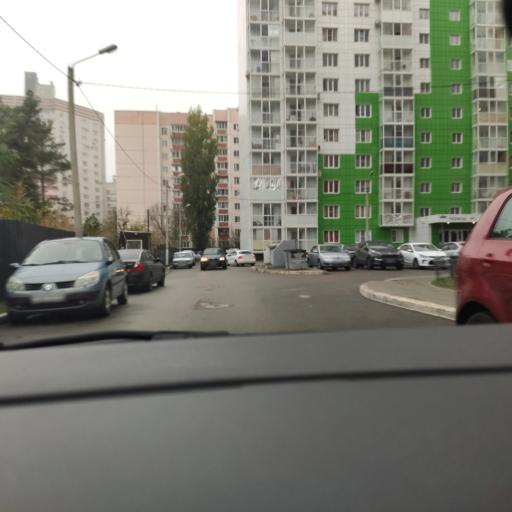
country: RU
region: Voronezj
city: Podgornoye
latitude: 51.6858
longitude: 39.1343
